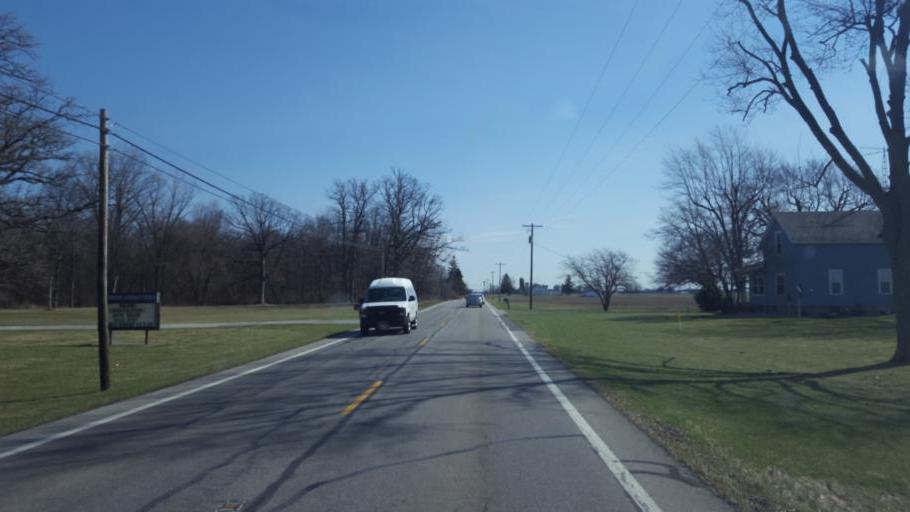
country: US
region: Ohio
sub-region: Marion County
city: Marion
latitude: 40.5819
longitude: -83.0501
